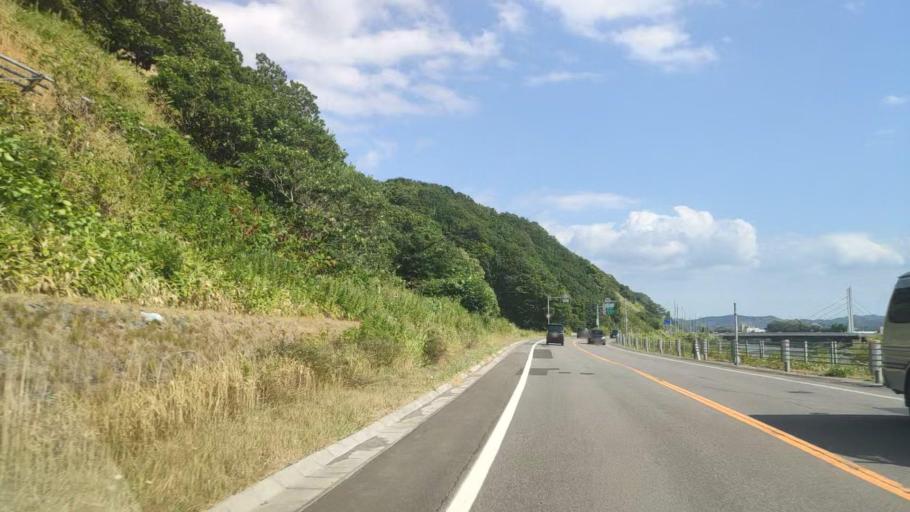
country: JP
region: Hokkaido
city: Rumoi
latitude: 43.9506
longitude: 141.6467
